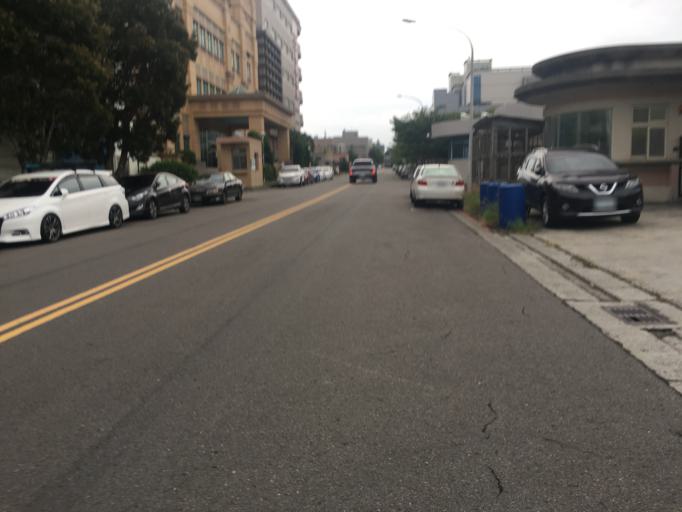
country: TW
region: Taiwan
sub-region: Hsinchu
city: Hsinchu
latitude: 24.7267
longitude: 120.9108
